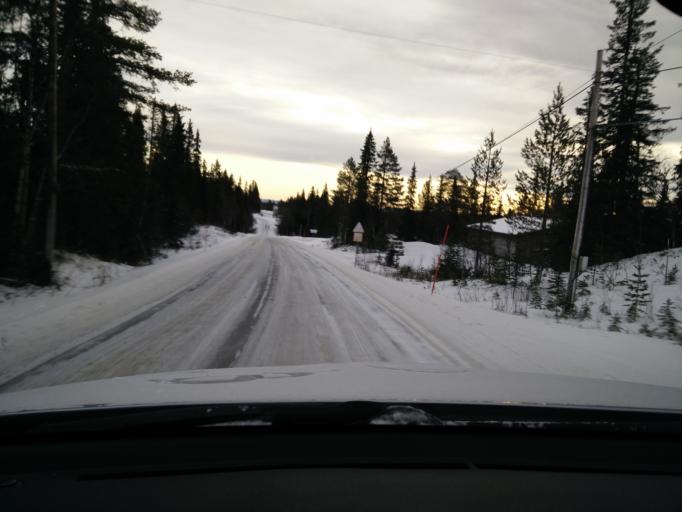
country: SE
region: Jaemtland
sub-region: Bergs Kommun
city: Hoverberg
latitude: 62.4800
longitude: 14.1250
